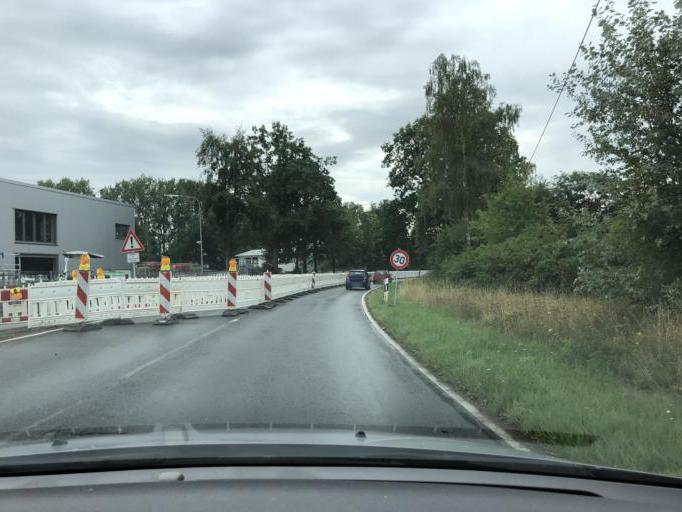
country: DE
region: North Rhine-Westphalia
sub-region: Regierungsbezirk Dusseldorf
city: Schermbeck
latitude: 51.6791
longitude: 6.8621
